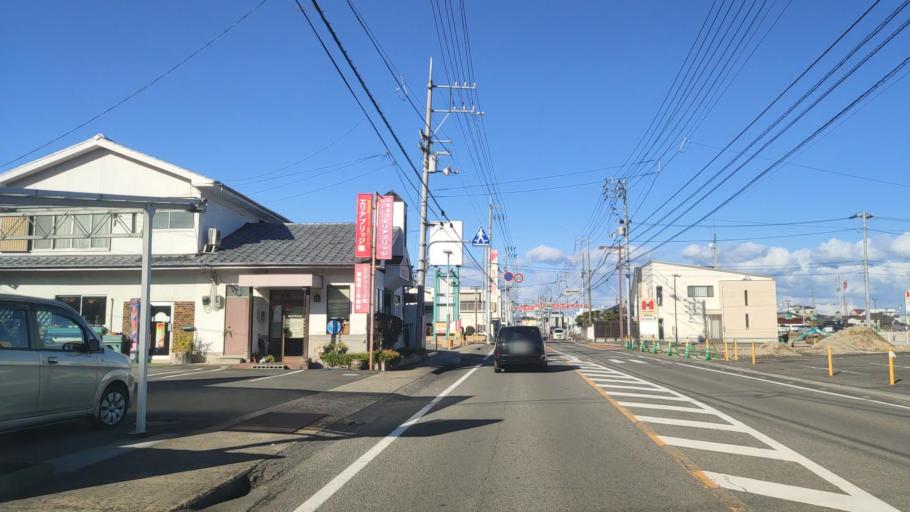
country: JP
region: Ehime
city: Saijo
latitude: 33.9188
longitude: 133.1918
